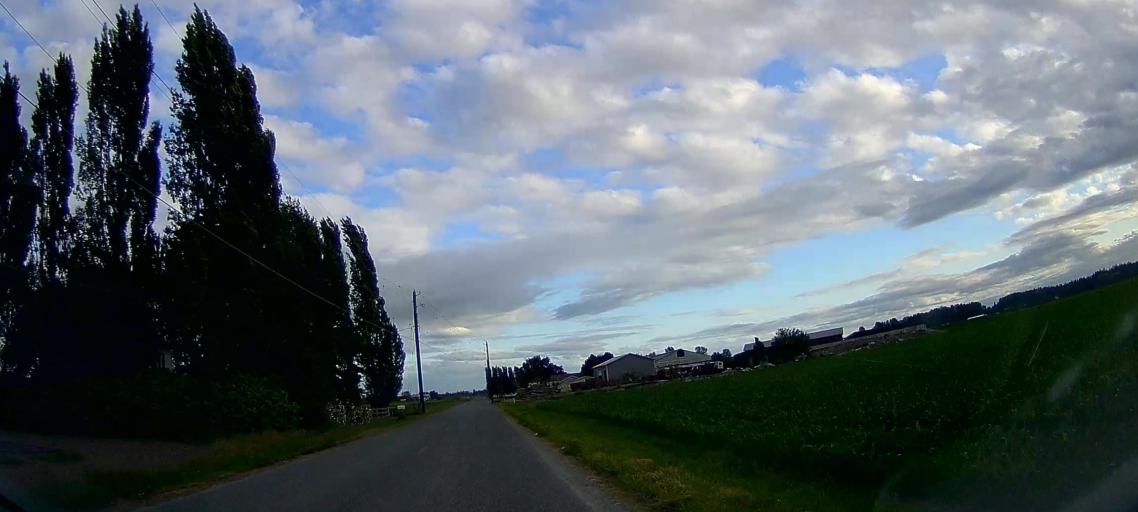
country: US
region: Washington
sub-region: Skagit County
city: Mount Vernon
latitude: 48.3770
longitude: -122.4007
